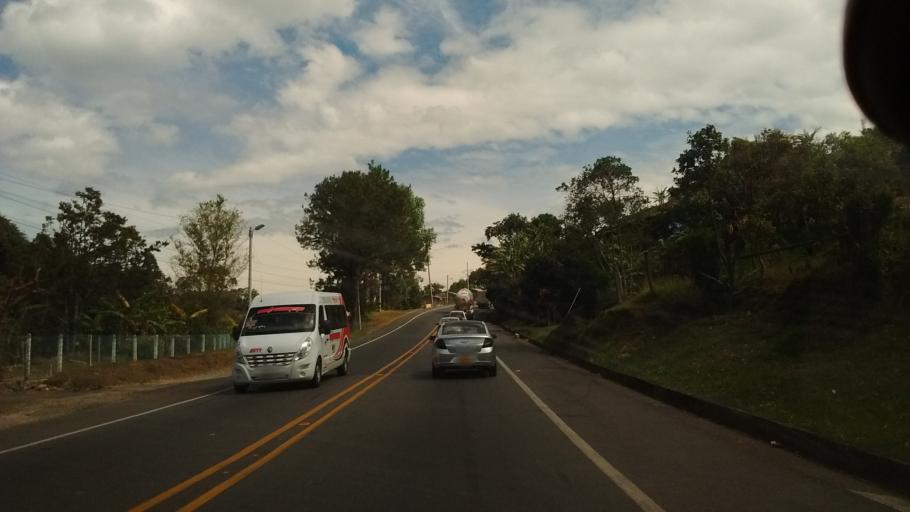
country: CO
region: Cauca
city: Cajibio
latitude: 2.6263
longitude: -76.5236
